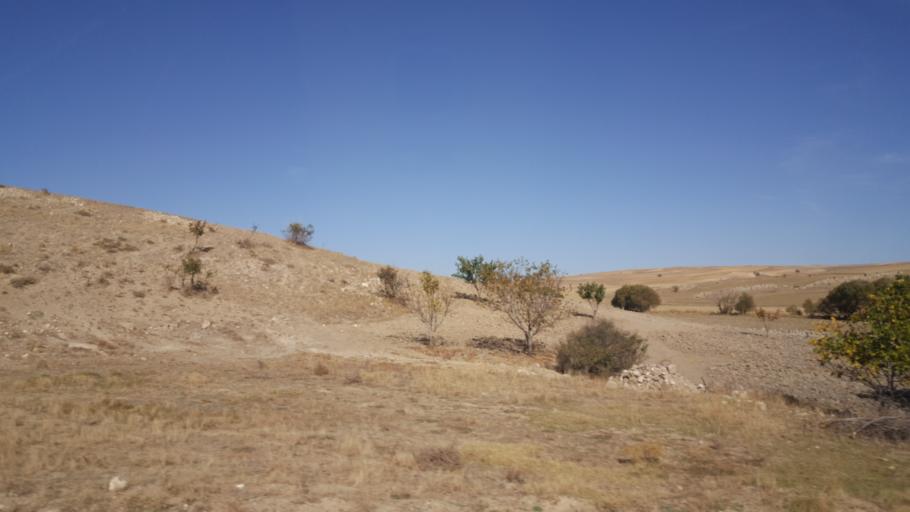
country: TR
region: Ankara
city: Haymana
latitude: 39.4202
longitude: 32.5940
